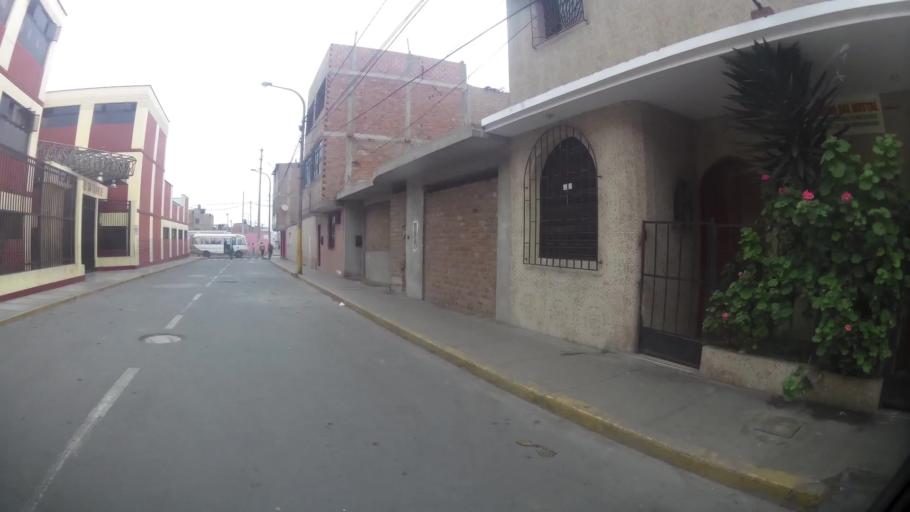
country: PE
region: Lima
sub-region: Provincia de Huaral
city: Chancay
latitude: -11.5605
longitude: -77.2686
